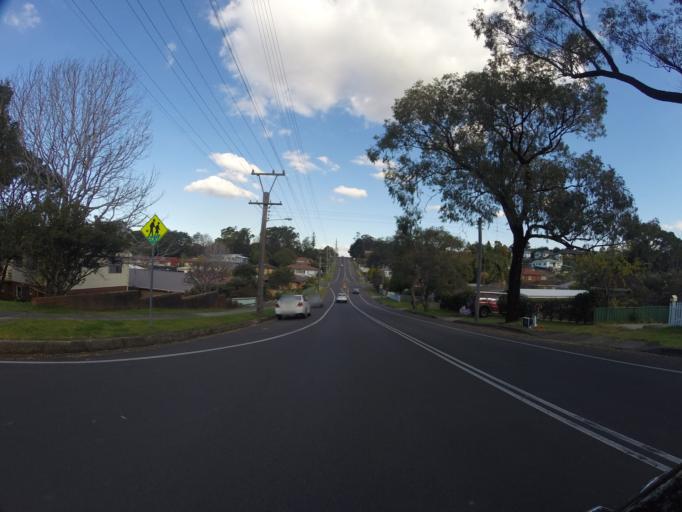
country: AU
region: New South Wales
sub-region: Wollongong
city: Keiraville
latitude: -34.4174
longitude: 150.8698
